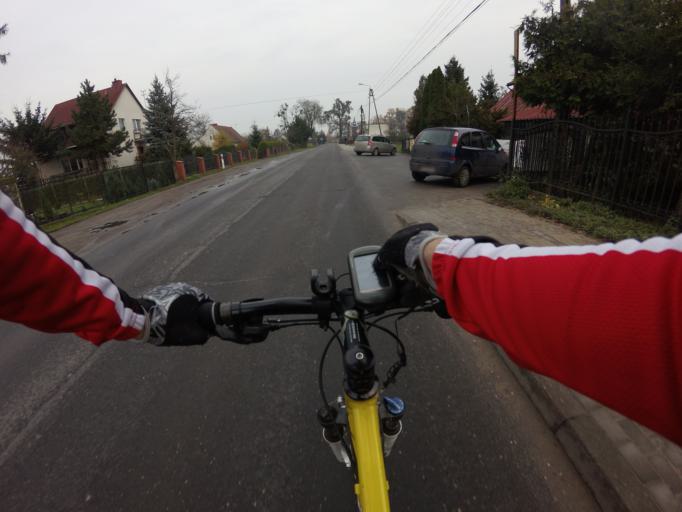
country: PL
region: Kujawsko-Pomorskie
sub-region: Powiat bydgoski
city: Osielsko
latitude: 53.2156
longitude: 18.0559
